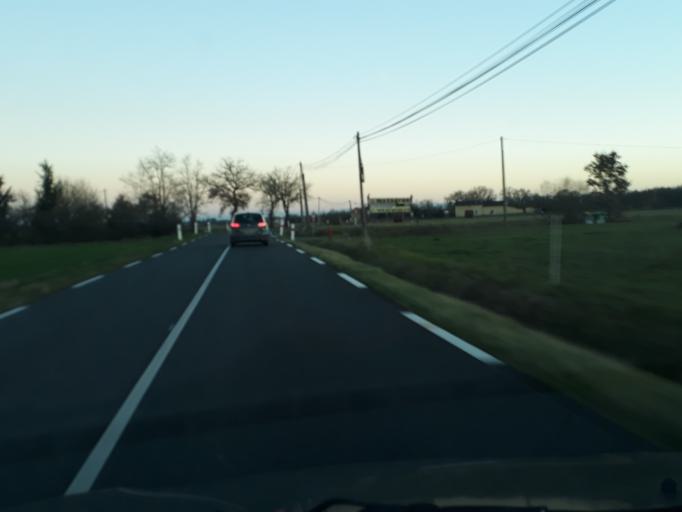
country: FR
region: Midi-Pyrenees
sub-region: Departement de la Haute-Garonne
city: Saint-Lys
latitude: 43.5306
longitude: 1.1709
